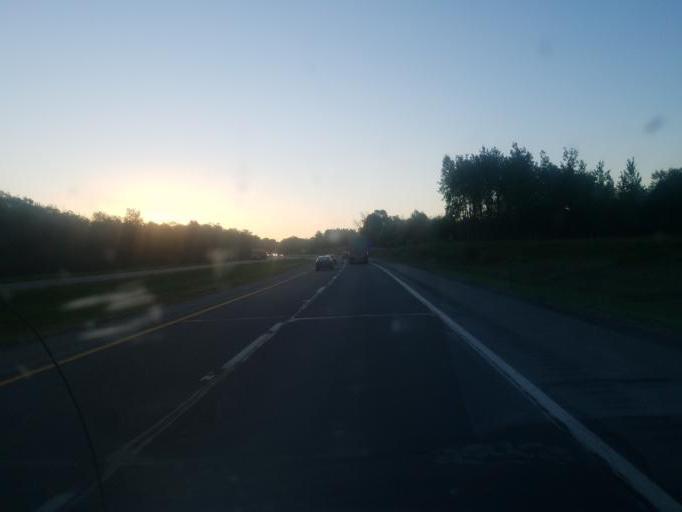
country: US
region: Ohio
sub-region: Mahoning County
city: New Middletown
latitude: 40.9480
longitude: -80.6293
